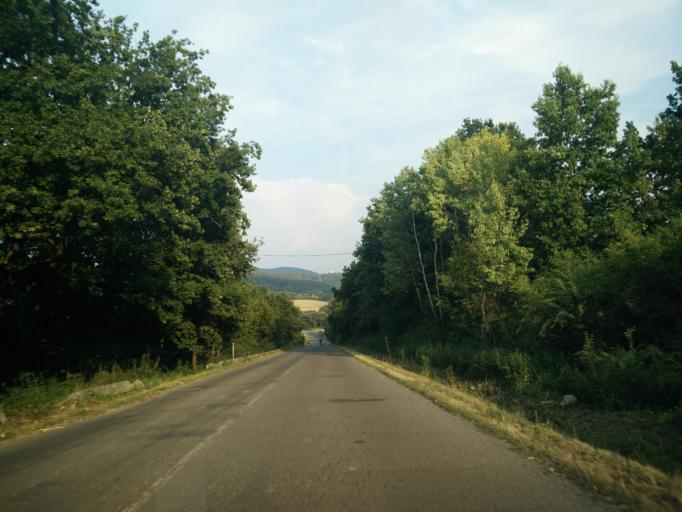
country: SK
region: Banskobystricky
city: Ziar nad Hronom
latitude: 48.6094
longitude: 18.8333
